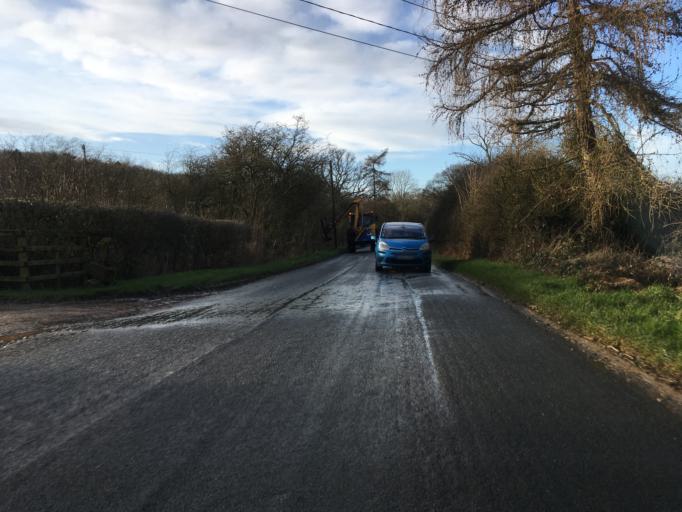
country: GB
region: England
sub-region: Warwickshire
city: Henley in Arden
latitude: 52.2217
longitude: -1.7886
